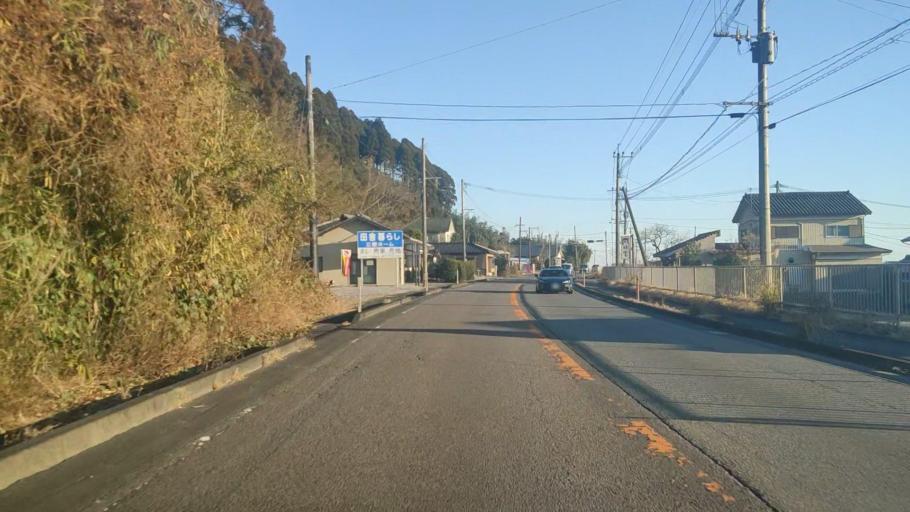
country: JP
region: Miyazaki
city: Takanabe
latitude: 32.0839
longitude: 131.5106
